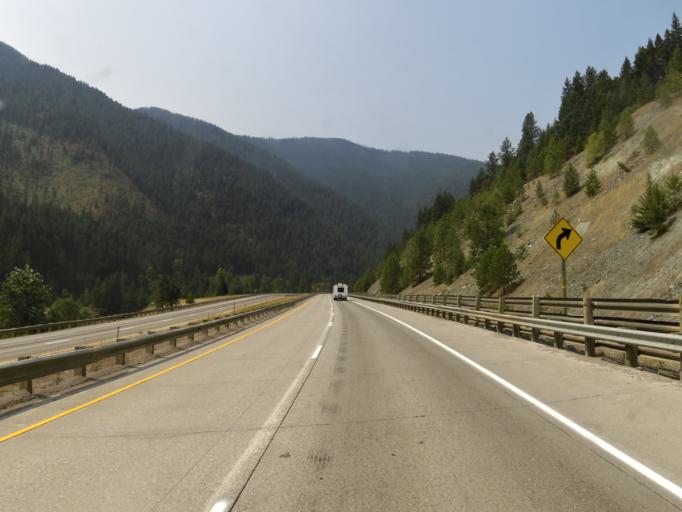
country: US
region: Montana
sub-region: Mineral County
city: Superior
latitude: 47.3026
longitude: -115.1933
